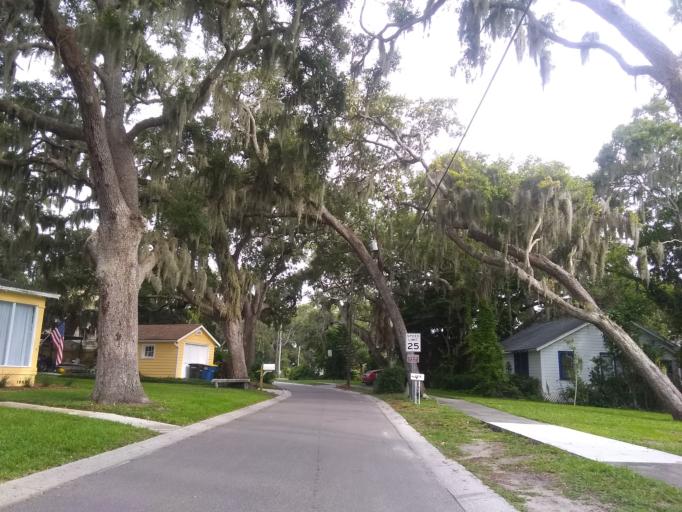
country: US
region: Florida
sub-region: Pinellas County
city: Clearwater
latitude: 27.9900
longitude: -82.7922
